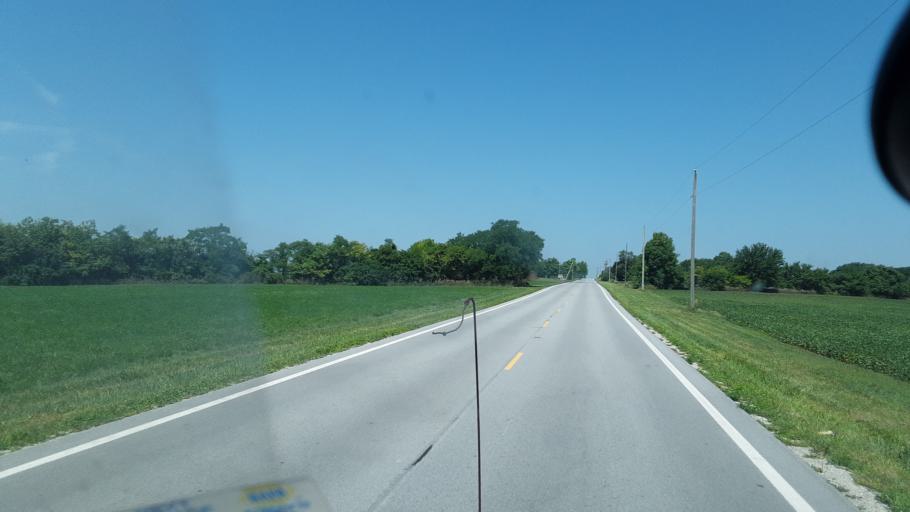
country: US
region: Ohio
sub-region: Wyandot County
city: Carey
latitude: 40.9827
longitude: -83.4471
